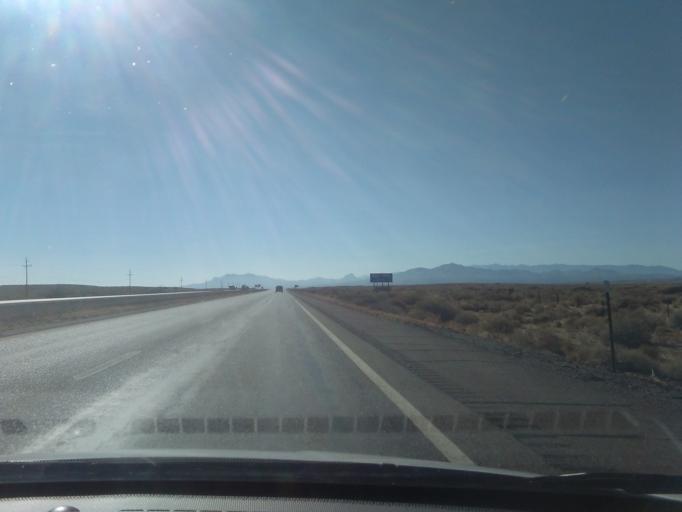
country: US
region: New Mexico
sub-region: Socorro County
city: Socorro
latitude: 34.3212
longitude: -106.8836
